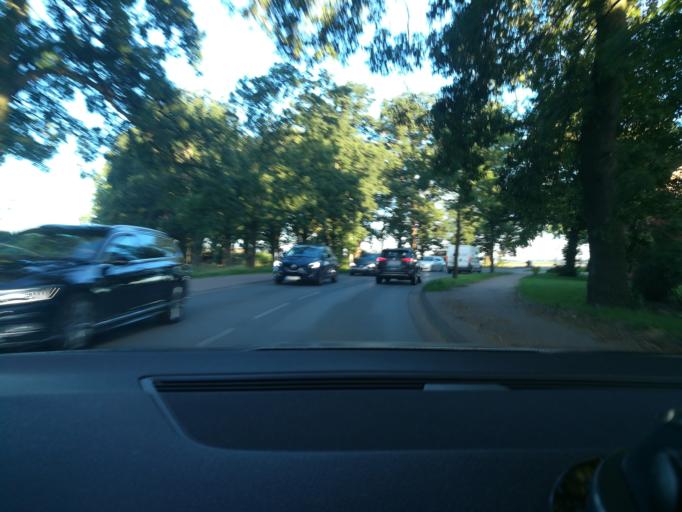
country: DE
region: North Rhine-Westphalia
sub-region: Regierungsbezirk Detmold
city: Minden
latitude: 52.3379
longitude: 8.8715
